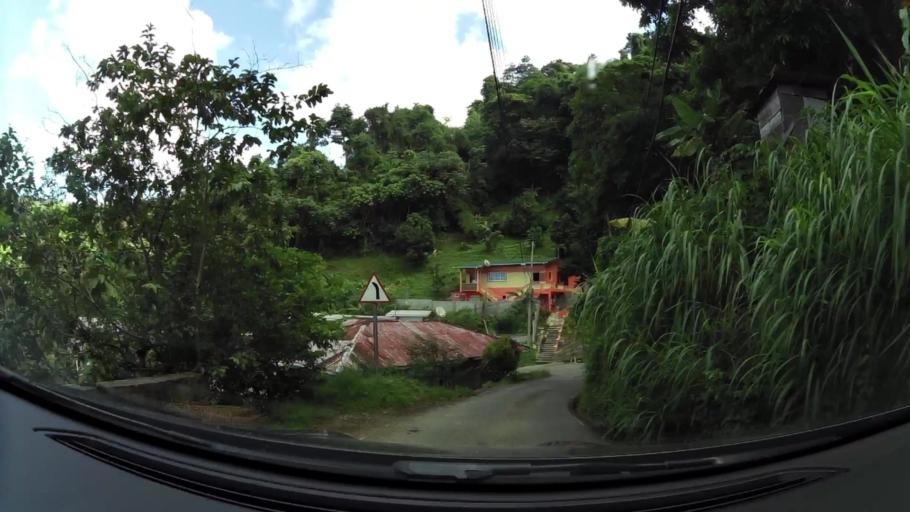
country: TT
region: Eastern Tobago
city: Roxborough
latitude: 11.3181
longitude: -60.5531
